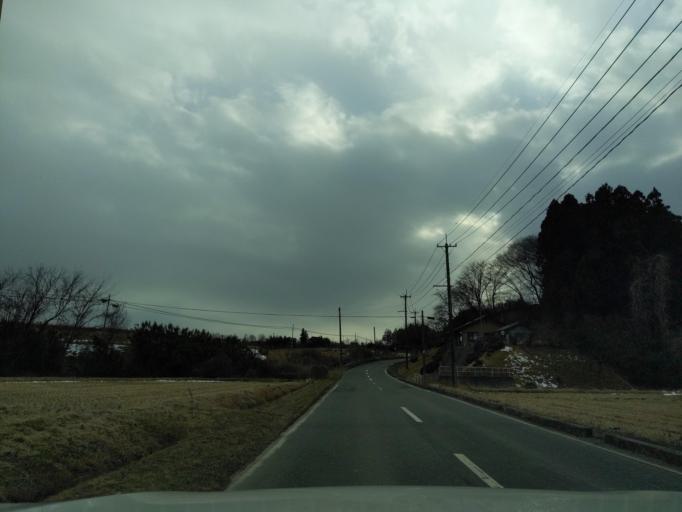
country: JP
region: Fukushima
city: Motomiya
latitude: 37.4573
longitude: 140.4055
